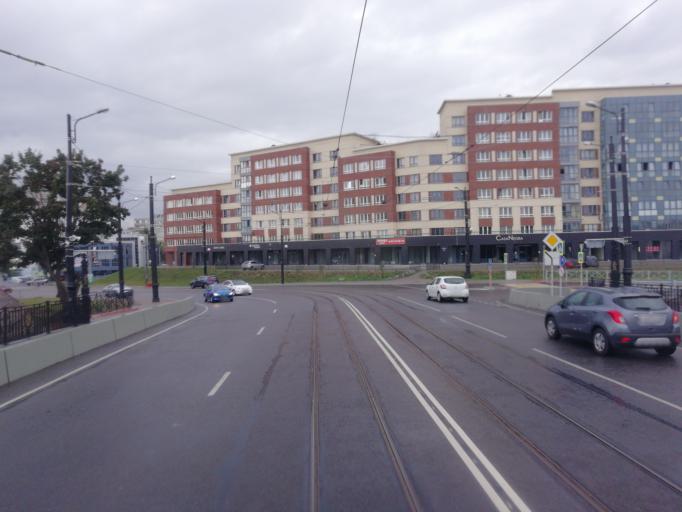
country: RU
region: Kaliningrad
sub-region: Gorod Kaliningrad
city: Kaliningrad
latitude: 54.6994
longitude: 20.5178
